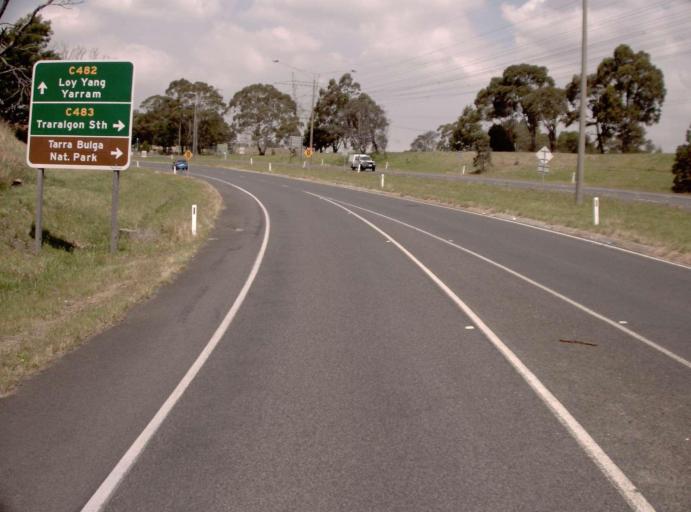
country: AU
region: Victoria
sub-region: Latrobe
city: Traralgon
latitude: -38.2490
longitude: 146.5489
